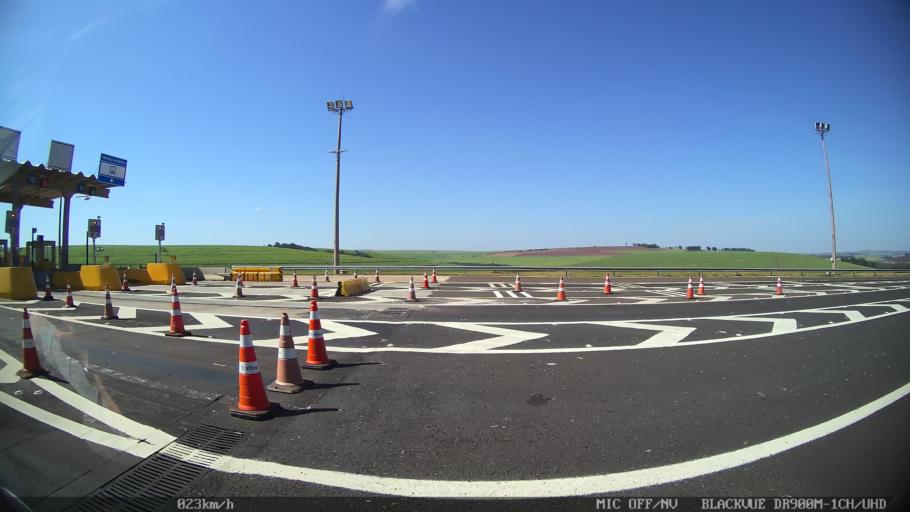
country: BR
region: Sao Paulo
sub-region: Batatais
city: Batatais
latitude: -20.7145
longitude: -47.5061
